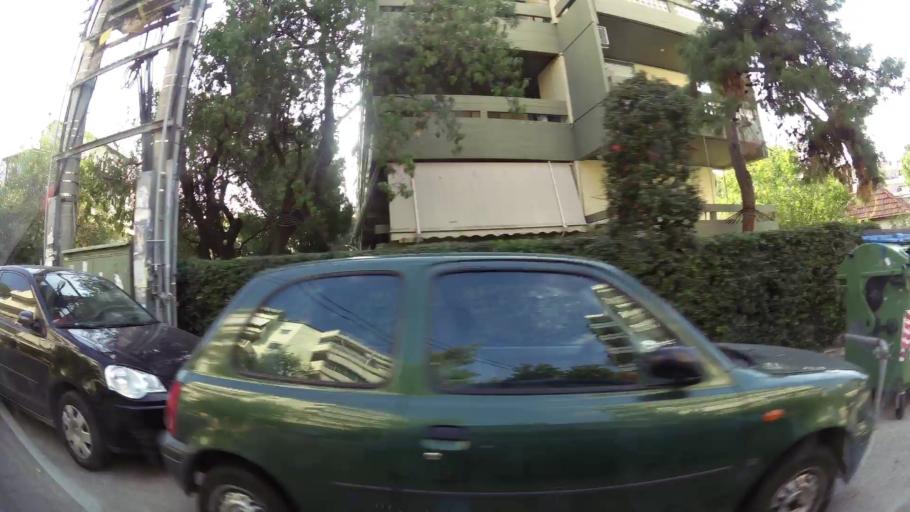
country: GR
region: Attica
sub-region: Nomarchia Athinas
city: Cholargos
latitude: 38.0089
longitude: 23.8129
